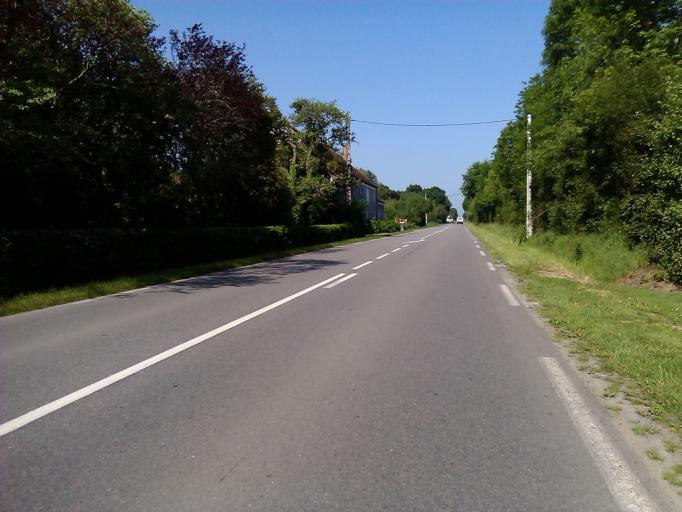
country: FR
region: Centre
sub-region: Departement de l'Indre
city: Neuvy-Saint-Sepulchre
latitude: 46.5979
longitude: 1.7950
